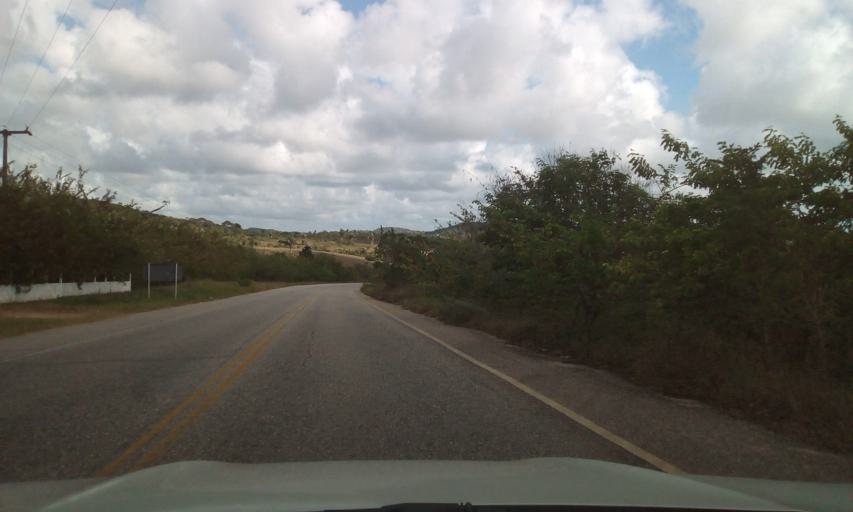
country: BR
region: Sergipe
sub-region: Indiaroba
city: Indiaroba
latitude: -11.4541
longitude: -37.4973
